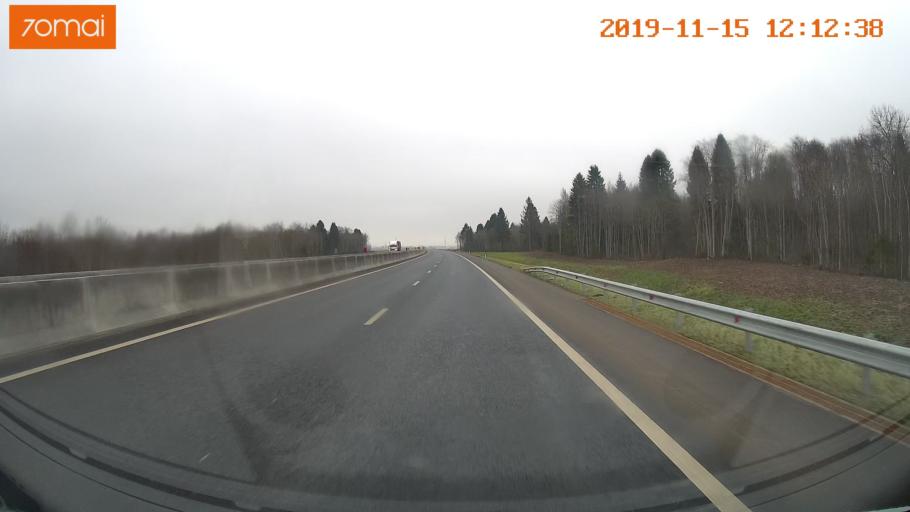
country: RU
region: Vologda
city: Vologda
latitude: 59.1734
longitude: 39.7703
